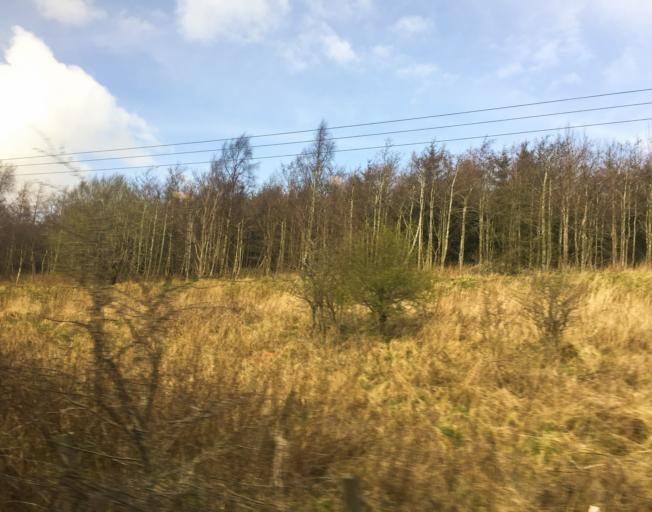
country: GB
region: Scotland
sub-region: North Lanarkshire
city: Glenboig
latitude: 55.8809
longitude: -4.0536
